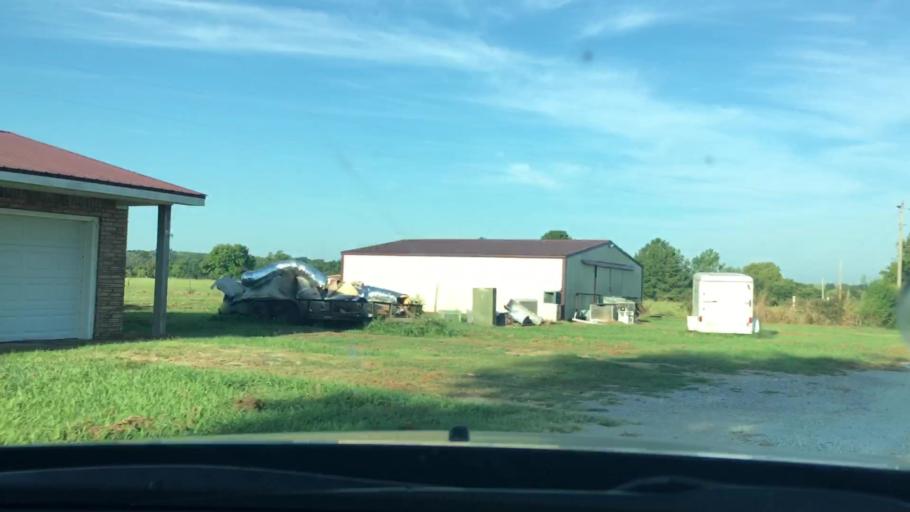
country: US
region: Oklahoma
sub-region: Pontotoc County
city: Ada
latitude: 34.6947
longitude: -96.4416
